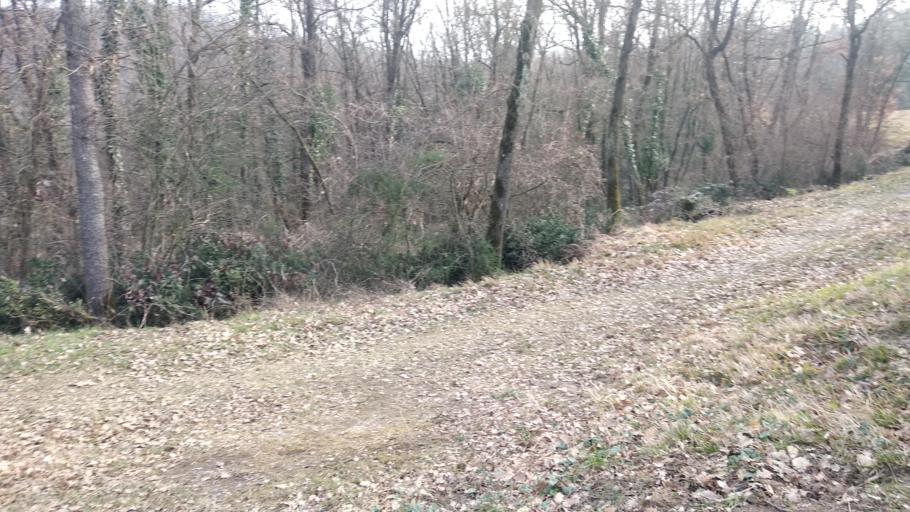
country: IT
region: Emilia-Romagna
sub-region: Provincia di Bologna
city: Ponticella
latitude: 44.4445
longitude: 11.3749
